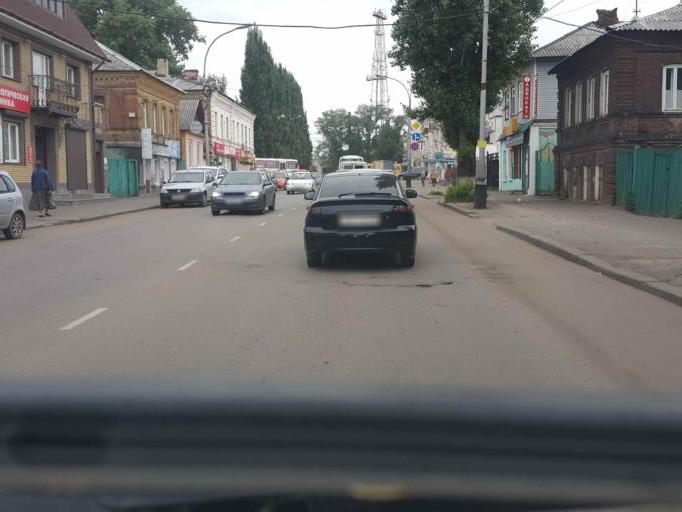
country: RU
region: Tambov
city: Michurinsk
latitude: 52.8933
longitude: 40.5006
